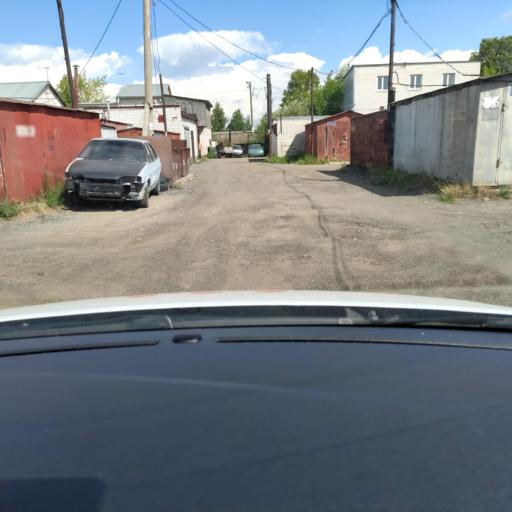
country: RU
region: Tatarstan
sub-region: Gorod Kazan'
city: Kazan
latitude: 55.8490
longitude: 49.1523
